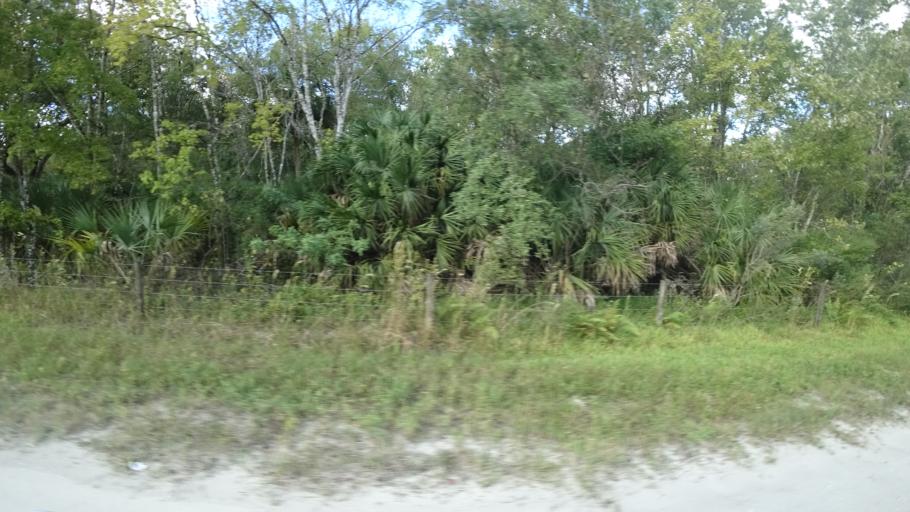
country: US
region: Florida
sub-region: Sarasota County
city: Lake Sarasota
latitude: 27.3374
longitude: -82.2052
